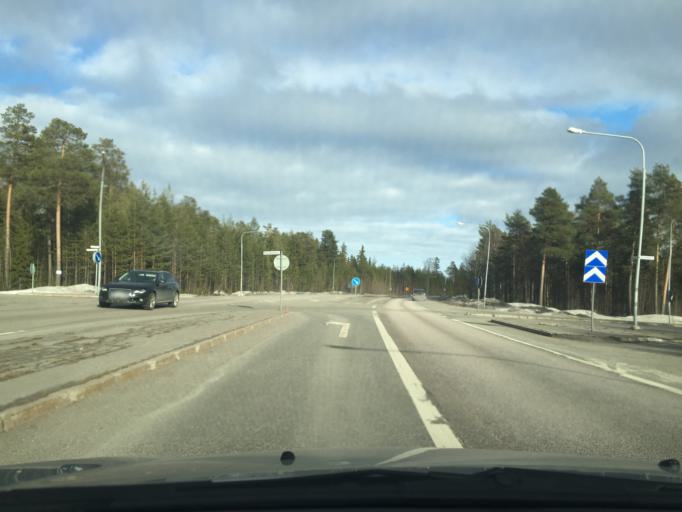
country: SE
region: Norrbotten
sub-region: Lulea Kommun
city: Lulea
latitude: 65.5926
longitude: 22.2426
